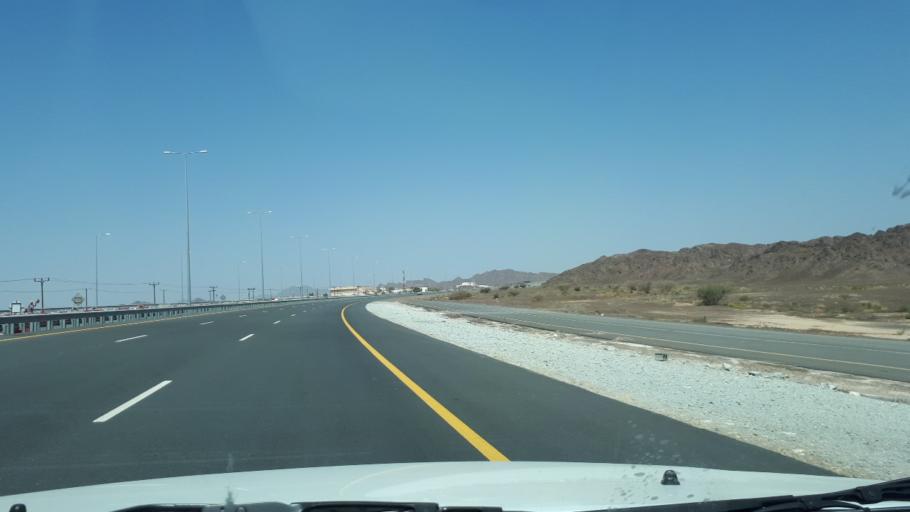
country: OM
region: Ash Sharqiyah
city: Ibra'
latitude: 22.6485
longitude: 58.6108
